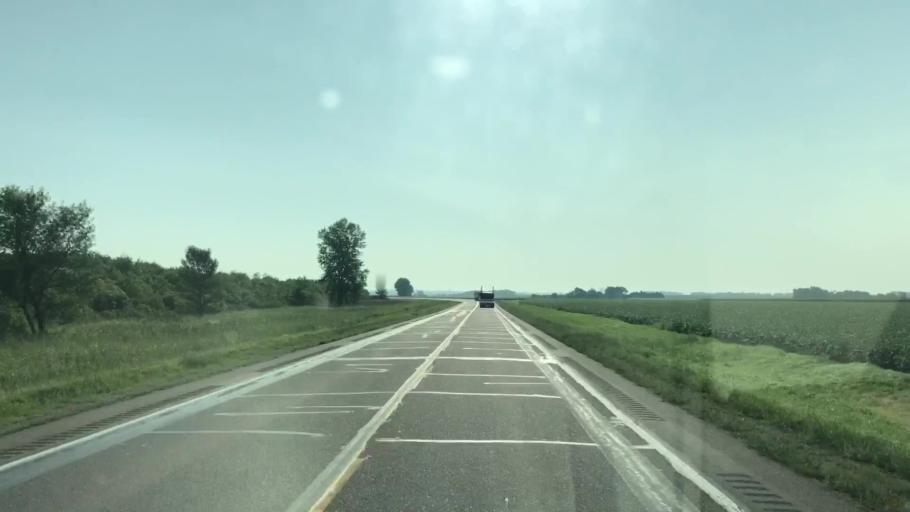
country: US
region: Iowa
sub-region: O'Brien County
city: Sheldon
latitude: 43.1853
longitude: -95.9580
